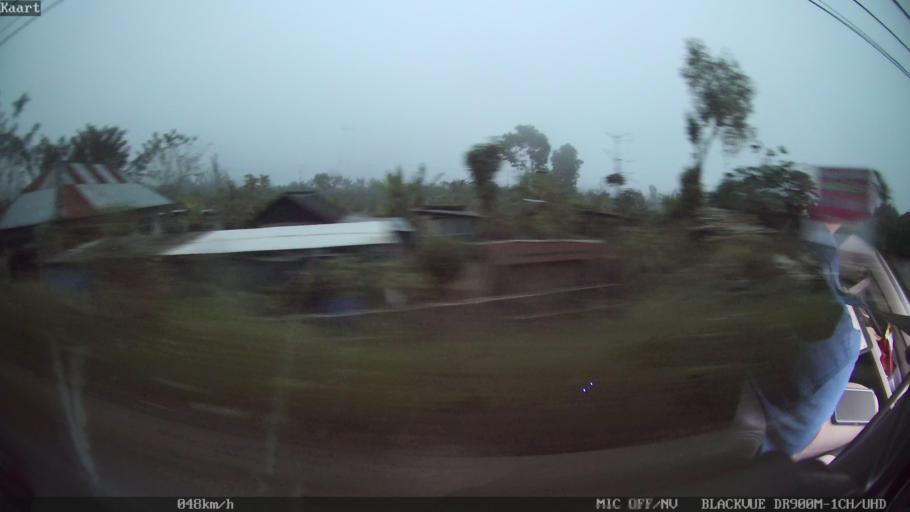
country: ID
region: Bali
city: Banjar Kedisan
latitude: -8.2922
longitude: 115.3164
